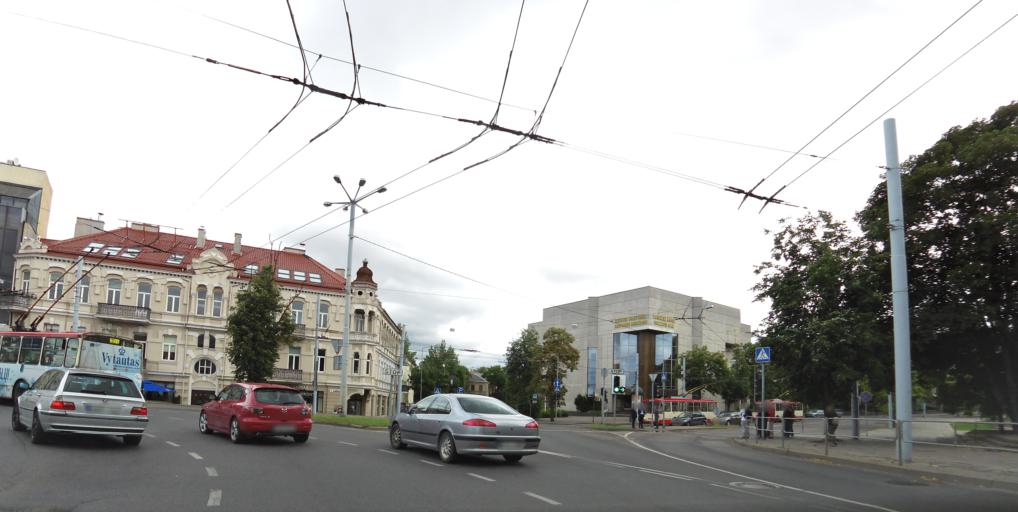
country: LT
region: Vilnius County
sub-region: Vilnius
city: Vilnius
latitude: 54.6902
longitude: 25.2794
